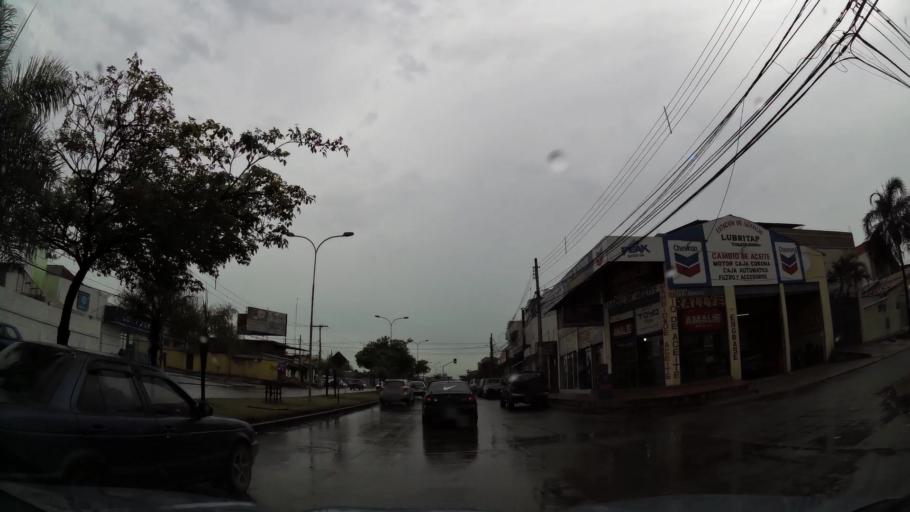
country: BO
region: Santa Cruz
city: Santa Cruz de la Sierra
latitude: -17.7692
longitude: -63.1545
